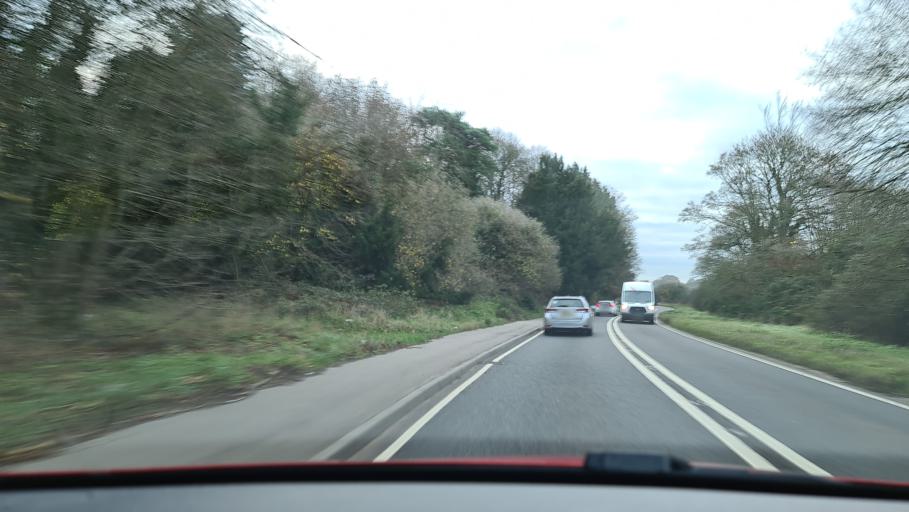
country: GB
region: England
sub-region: Buckinghamshire
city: Princes Risborough
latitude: 51.6629
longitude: -0.8080
